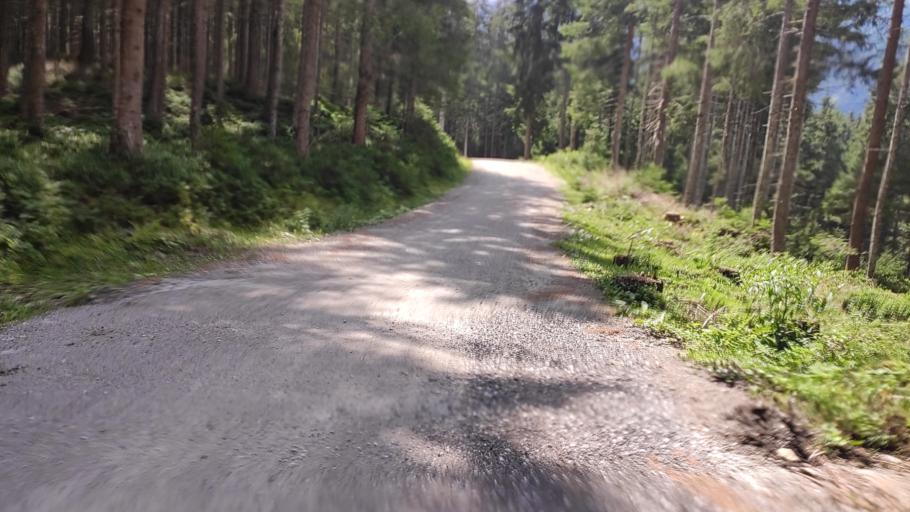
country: AT
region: Salzburg
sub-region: Politischer Bezirk Zell am See
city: Krimml
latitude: 47.2272
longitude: 12.1901
